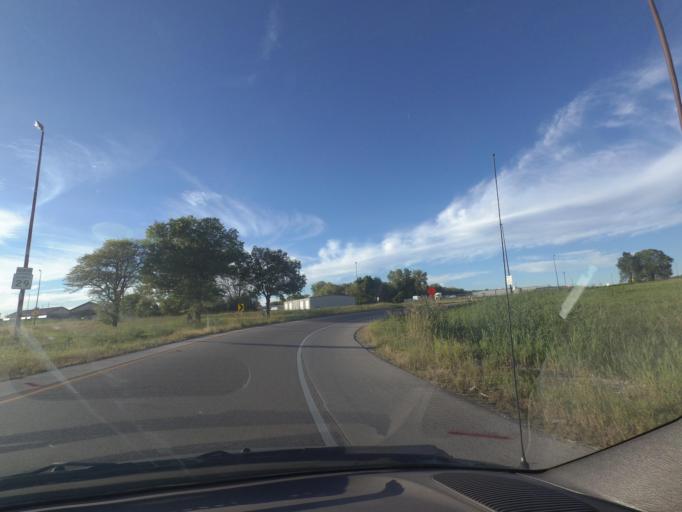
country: US
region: Illinois
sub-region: Sangamon County
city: Grandview
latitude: 39.7871
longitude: -89.6005
